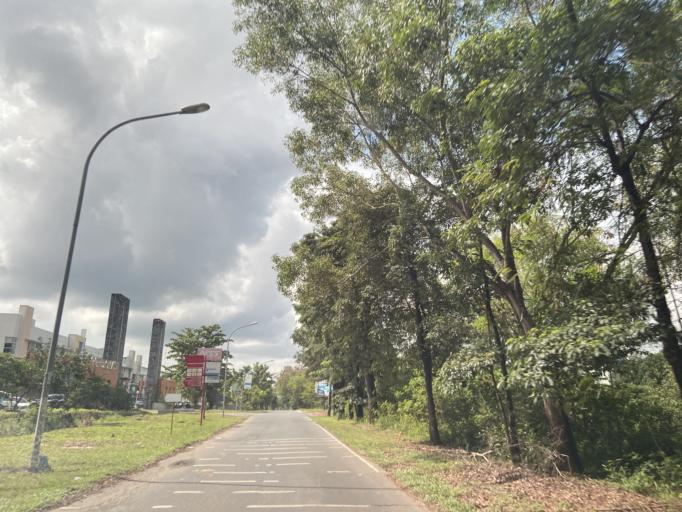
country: SG
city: Singapore
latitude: 1.1082
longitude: 104.0307
